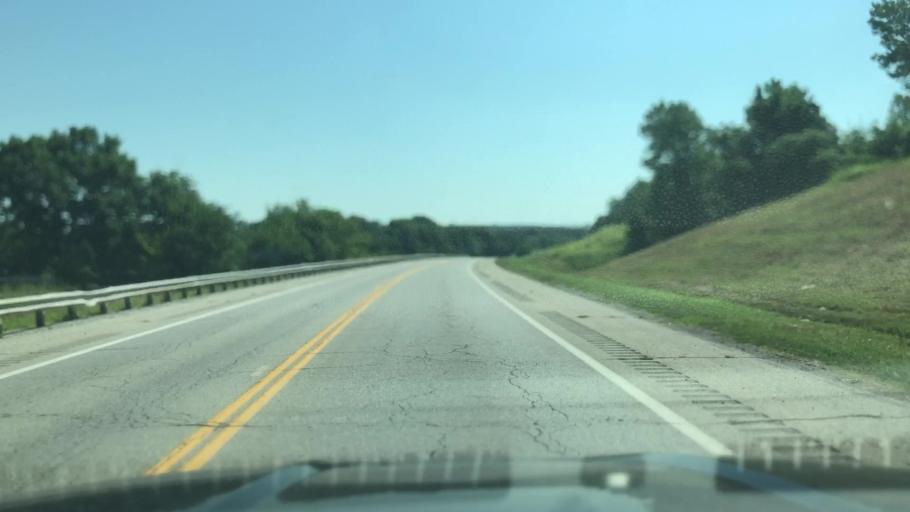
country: US
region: Oklahoma
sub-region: Creek County
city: Drumright
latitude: 35.9882
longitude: -96.5757
